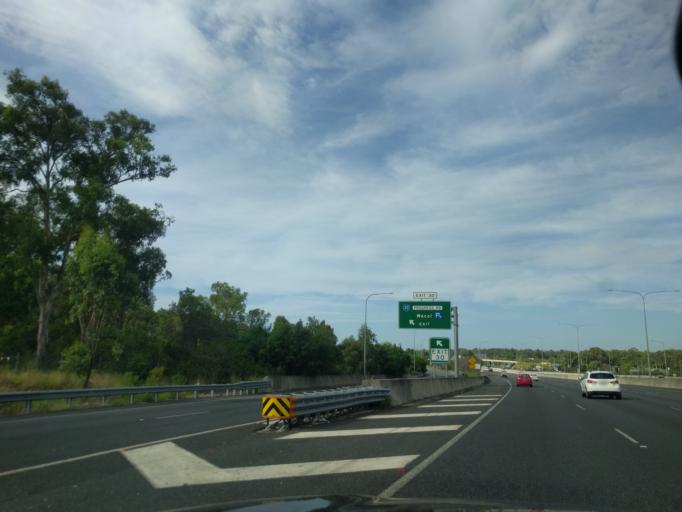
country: AU
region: Queensland
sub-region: Brisbane
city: Wacol
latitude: -27.5851
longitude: 152.9300
